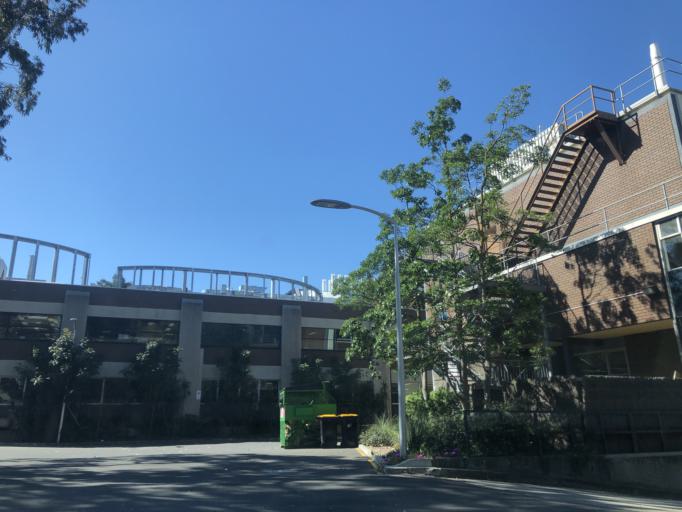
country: AU
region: Victoria
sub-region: Monash
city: Clayton
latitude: -37.9108
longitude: 145.1300
